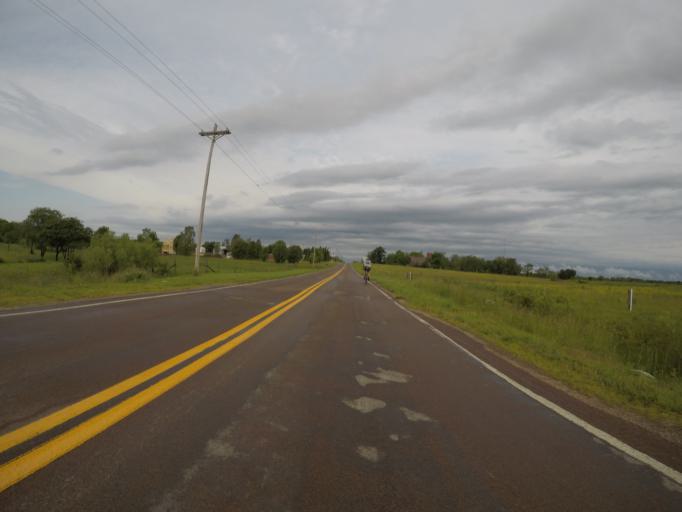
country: US
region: Kansas
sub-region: Shawnee County
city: Auburn
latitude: 38.9566
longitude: -95.8547
